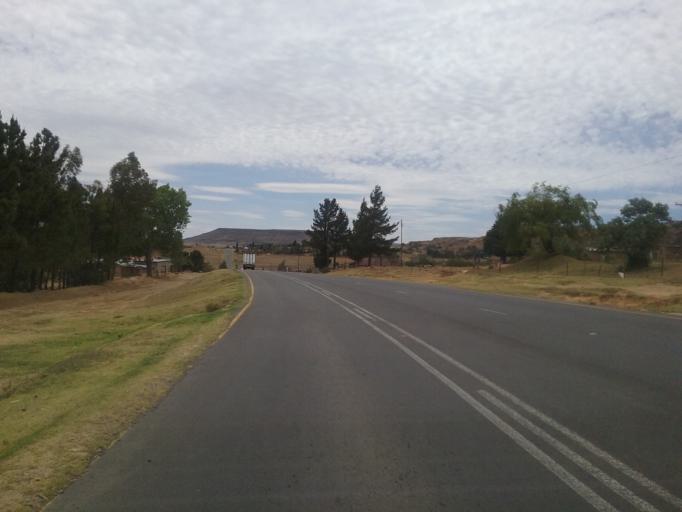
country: LS
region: Maseru
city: Nako
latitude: -29.6430
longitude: 27.4753
